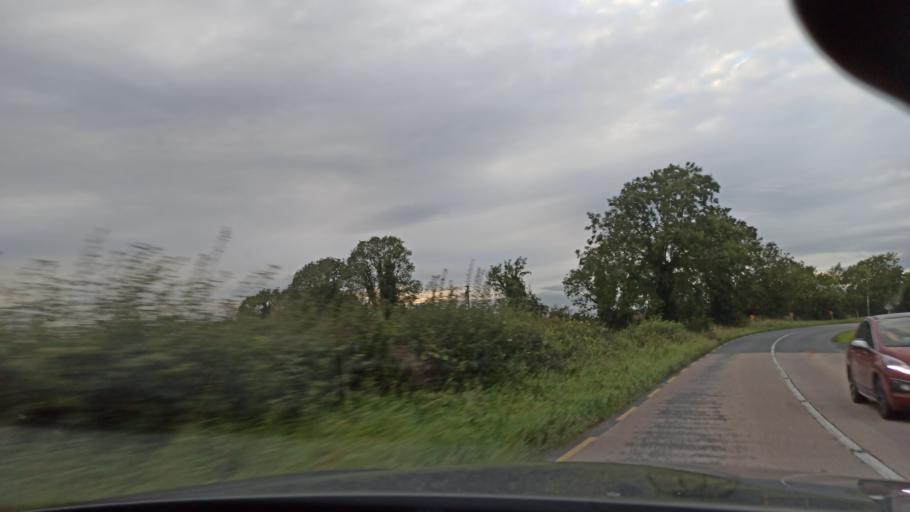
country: IE
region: Munster
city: Cashel
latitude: 52.4790
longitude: -7.8517
